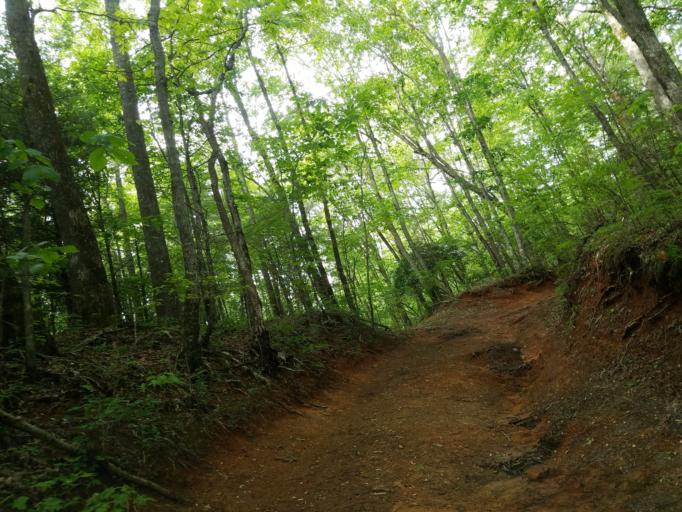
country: US
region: Georgia
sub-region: Union County
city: Blairsville
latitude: 34.7335
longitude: -84.0249
